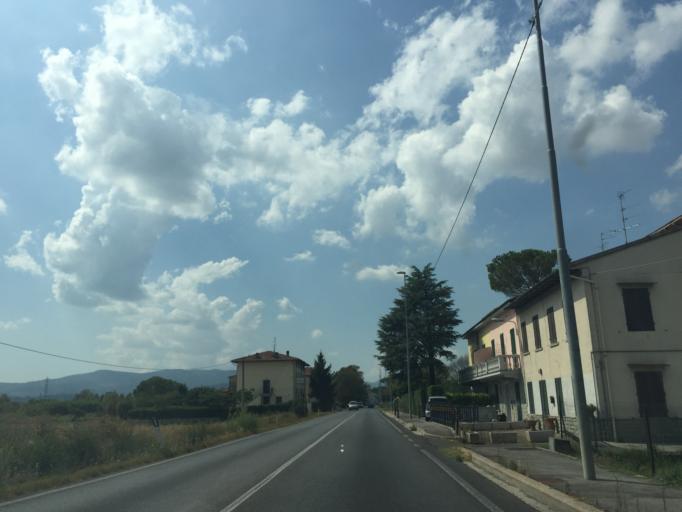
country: IT
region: Tuscany
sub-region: Province of Florence
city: Signa
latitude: 43.8087
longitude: 11.0947
